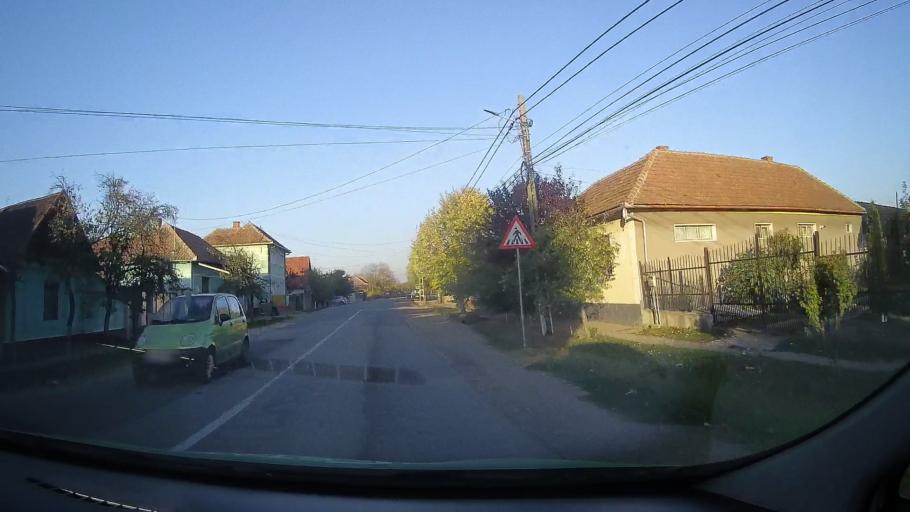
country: RO
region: Bihor
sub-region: Comuna Salard
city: Salard
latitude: 47.2200
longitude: 22.0368
